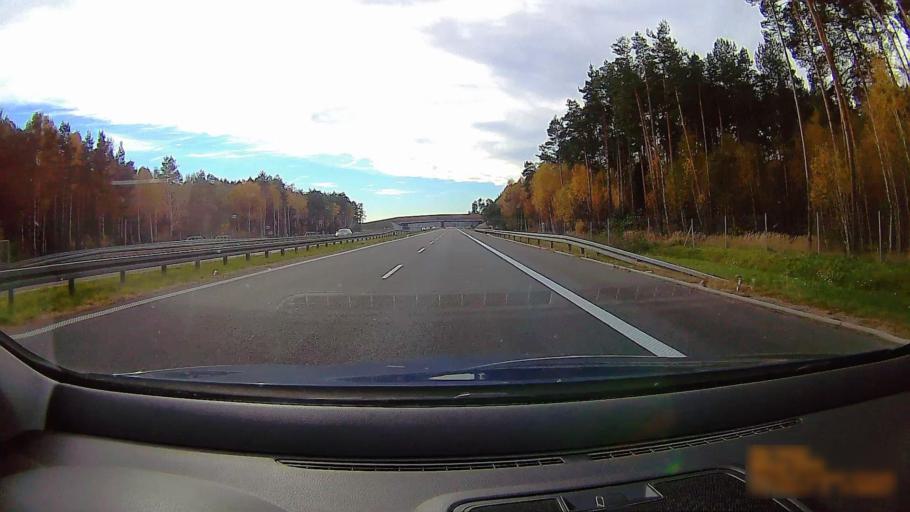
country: PL
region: Greater Poland Voivodeship
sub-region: Powiat ostrowski
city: Przygodzice
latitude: 51.5649
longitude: 17.8469
